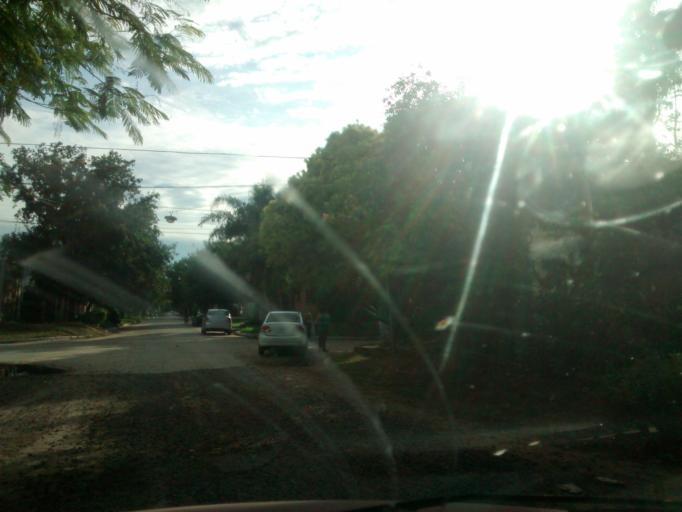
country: AR
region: Chaco
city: Resistencia
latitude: -27.4430
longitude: -58.9705
